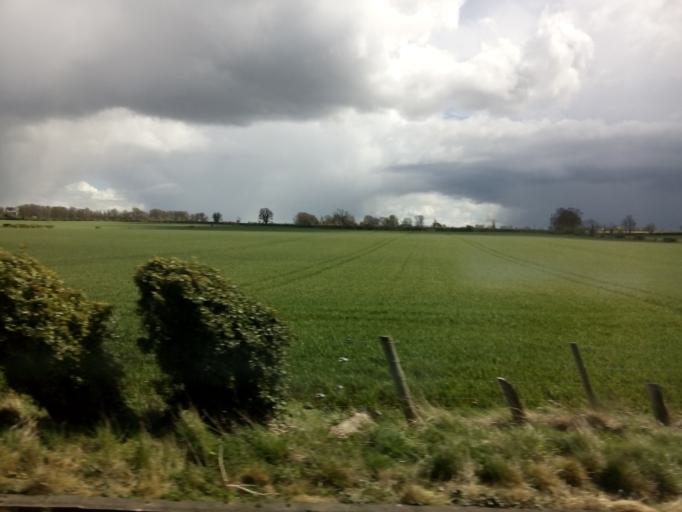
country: GB
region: Scotland
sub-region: East Lothian
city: Longniddry
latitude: 55.9699
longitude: -2.9028
